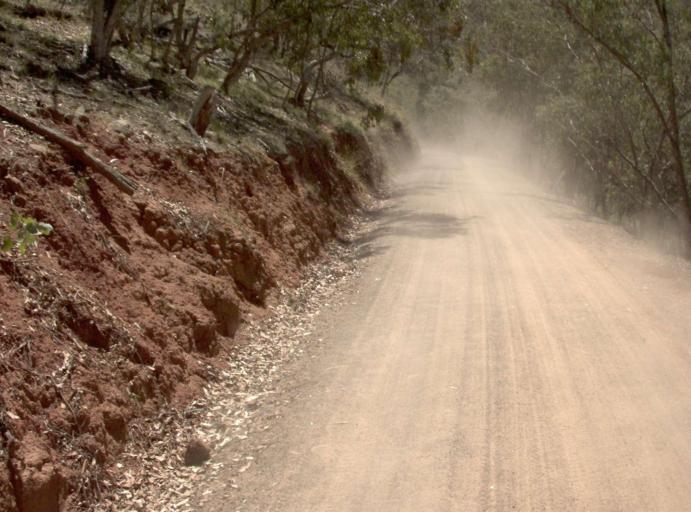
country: AU
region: New South Wales
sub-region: Snowy River
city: Jindabyne
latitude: -37.0787
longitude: 148.4566
